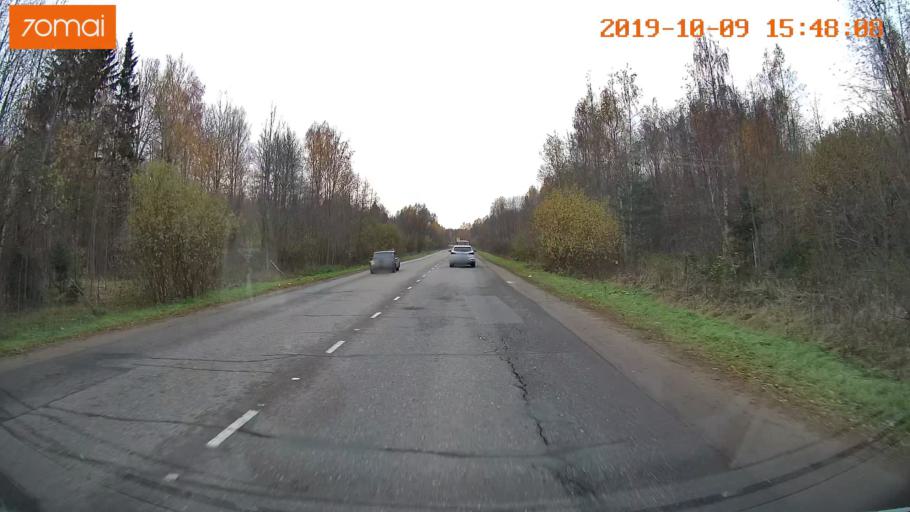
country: RU
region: Kostroma
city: Oktyabr'skiy
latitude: 57.8133
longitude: 41.0193
